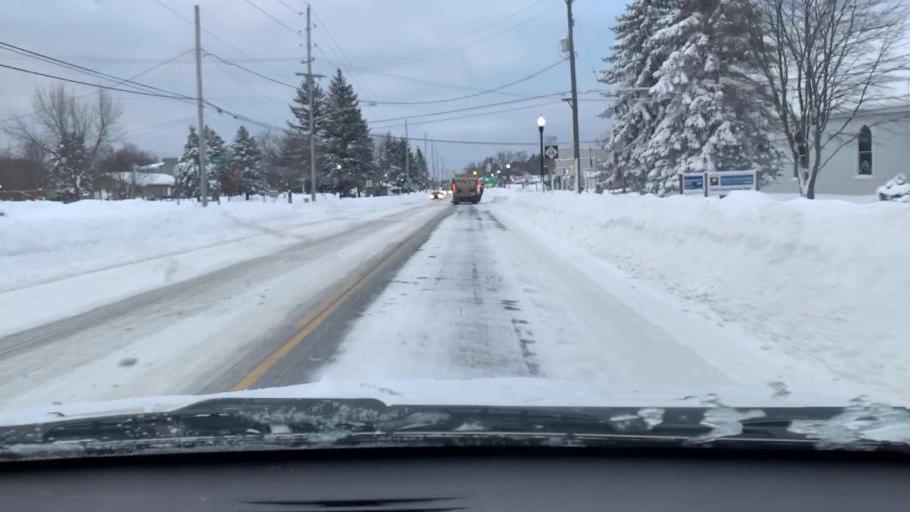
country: US
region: Michigan
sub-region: Antrim County
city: Mancelona
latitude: 44.9038
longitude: -85.0588
